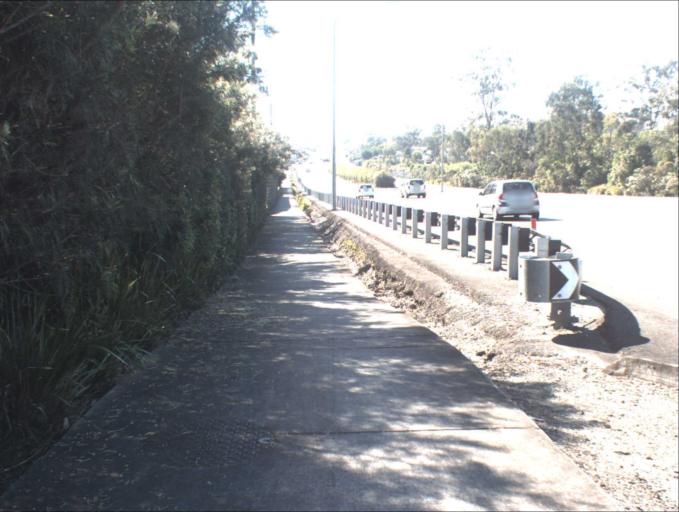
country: AU
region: Queensland
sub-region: Logan
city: Beenleigh
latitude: -27.7118
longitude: 153.1738
